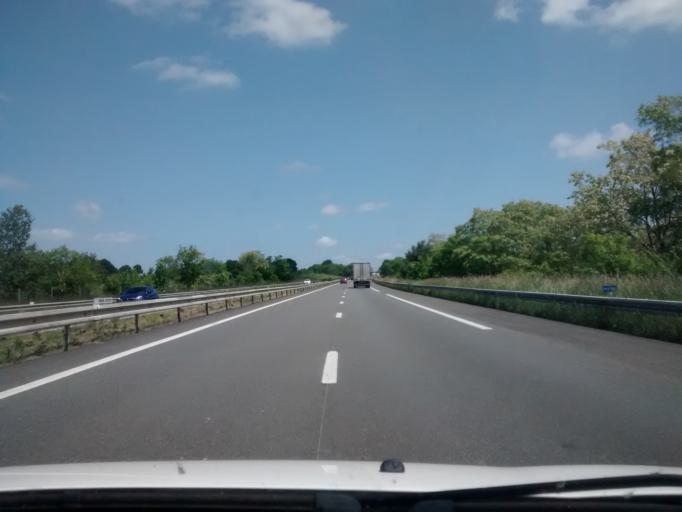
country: FR
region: Pays de la Loire
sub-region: Departement de la Sarthe
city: Coulans-sur-Gee
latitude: 48.0352
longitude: 0.0170
